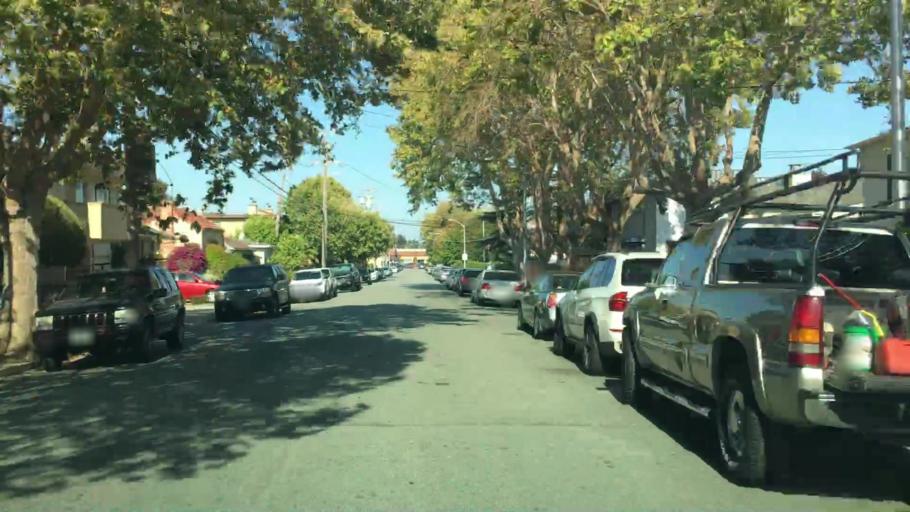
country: US
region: California
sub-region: San Mateo County
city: San Mateo
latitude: 37.5440
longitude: -122.3094
